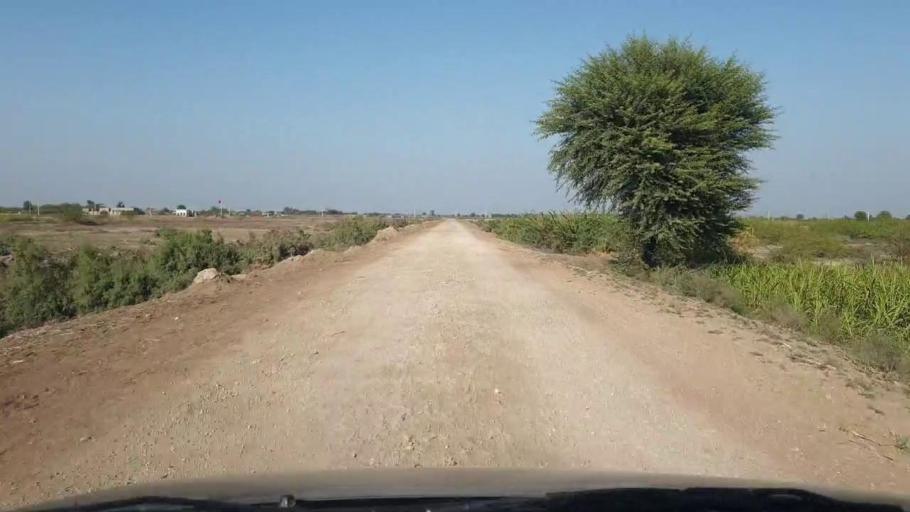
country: PK
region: Sindh
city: Digri
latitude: 25.1352
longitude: 69.2785
